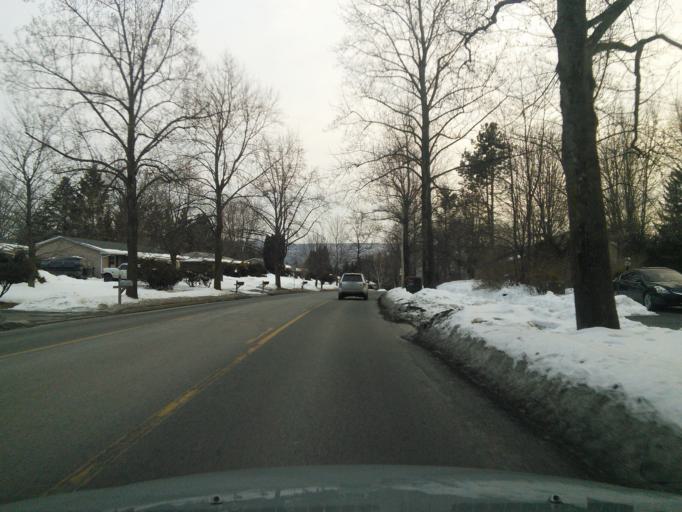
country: US
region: Pennsylvania
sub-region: Centre County
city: State College
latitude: 40.7903
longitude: -77.8387
